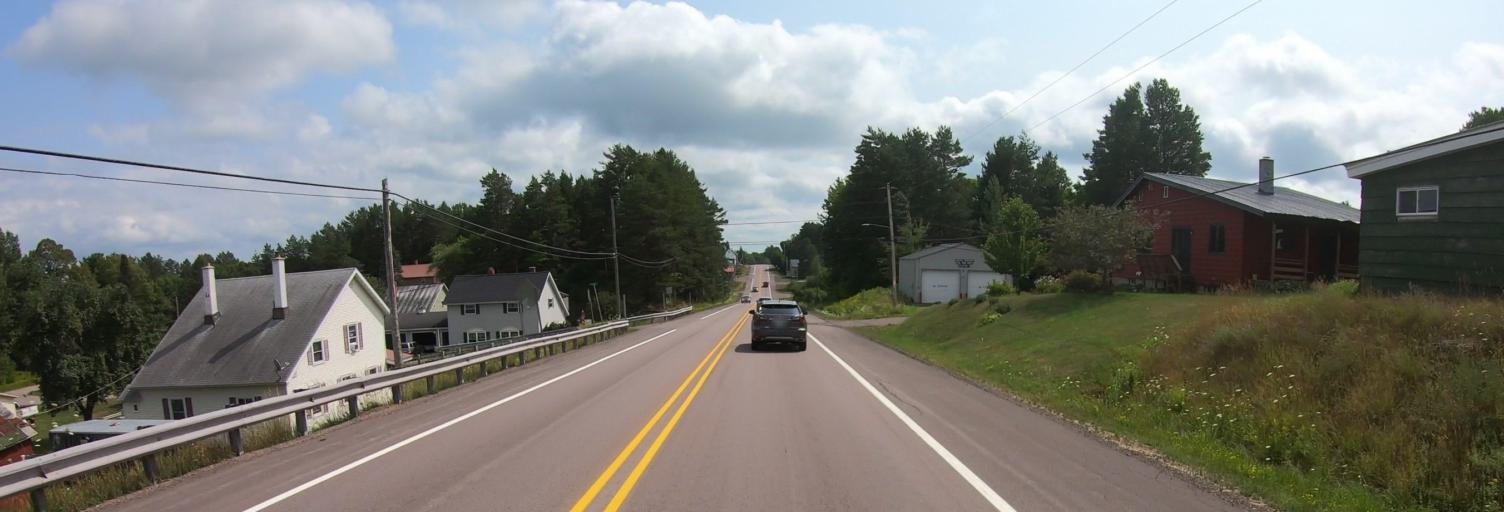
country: US
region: Michigan
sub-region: Houghton County
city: Hancock
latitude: 47.0457
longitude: -88.6726
